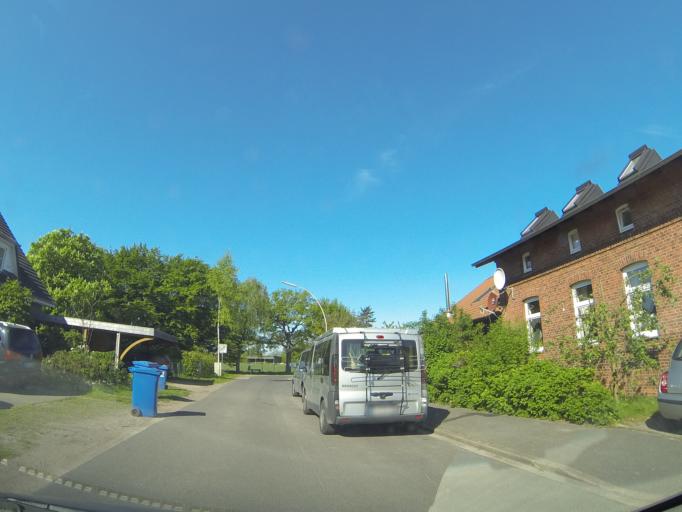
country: DE
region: Schleswig-Holstein
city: Halstenbek
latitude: 53.6299
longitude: 9.8314
